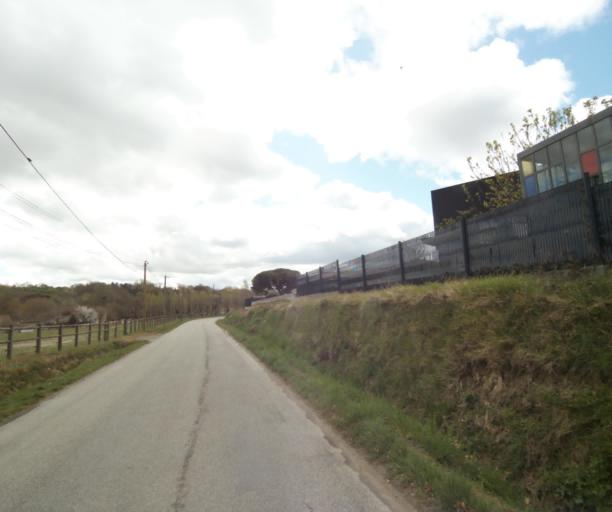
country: FR
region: Midi-Pyrenees
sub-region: Departement de l'Ariege
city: Saverdun
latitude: 43.2260
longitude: 1.5713
